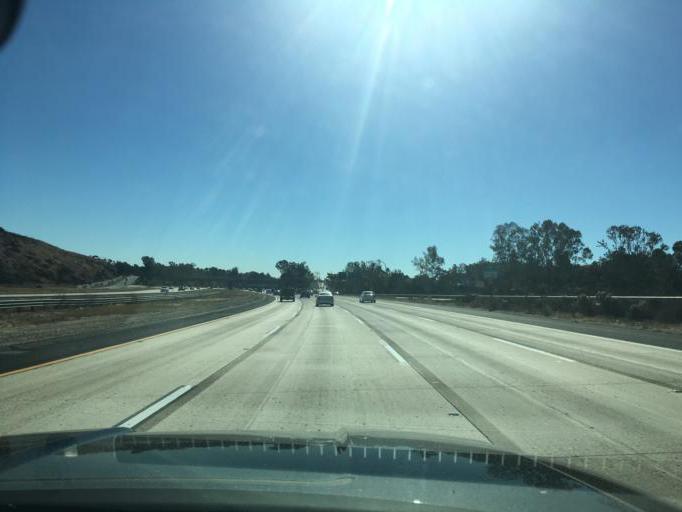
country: US
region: California
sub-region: San Diego County
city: La Mesa
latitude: 32.8383
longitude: -117.1210
